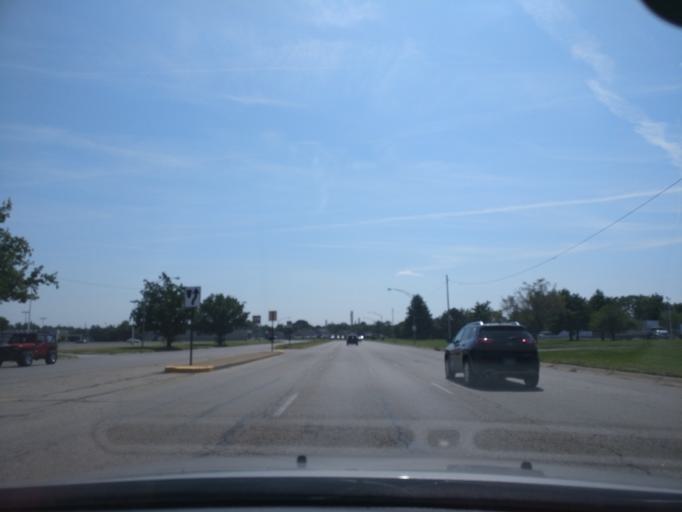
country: US
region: Ohio
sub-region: Butler County
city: Middletown
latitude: 39.4994
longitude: -84.3972
